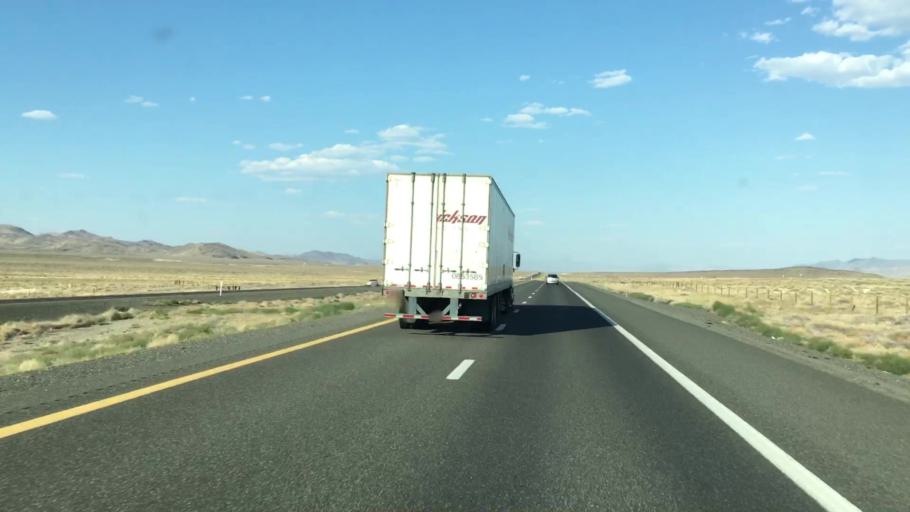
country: US
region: Nevada
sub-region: Lyon County
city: Fernley
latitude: 39.8466
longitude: -118.9370
